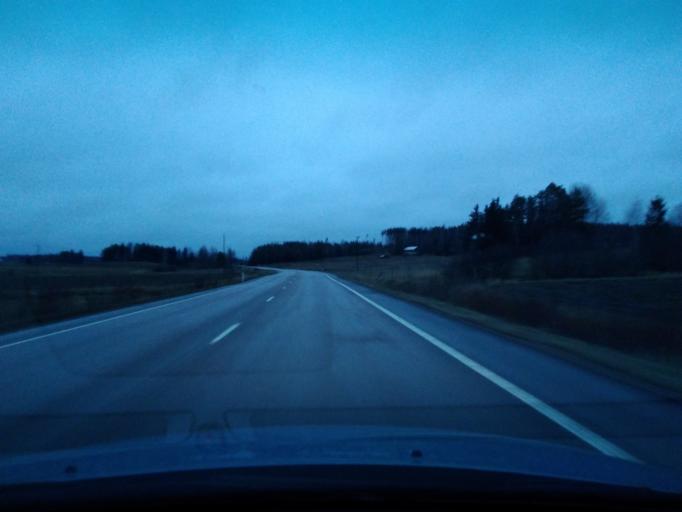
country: FI
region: Uusimaa
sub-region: Porvoo
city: Askola
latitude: 60.4624
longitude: 25.5778
